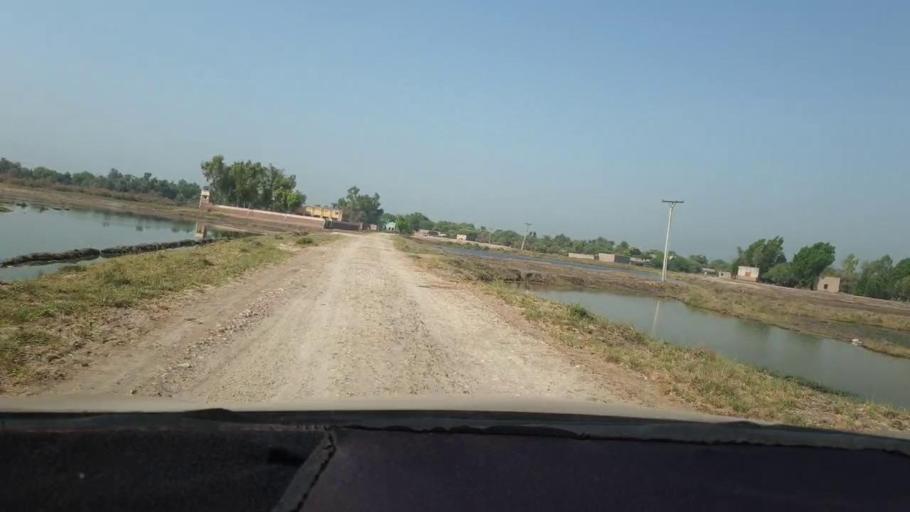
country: PK
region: Sindh
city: Miro Khan
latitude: 27.7081
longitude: 68.0978
